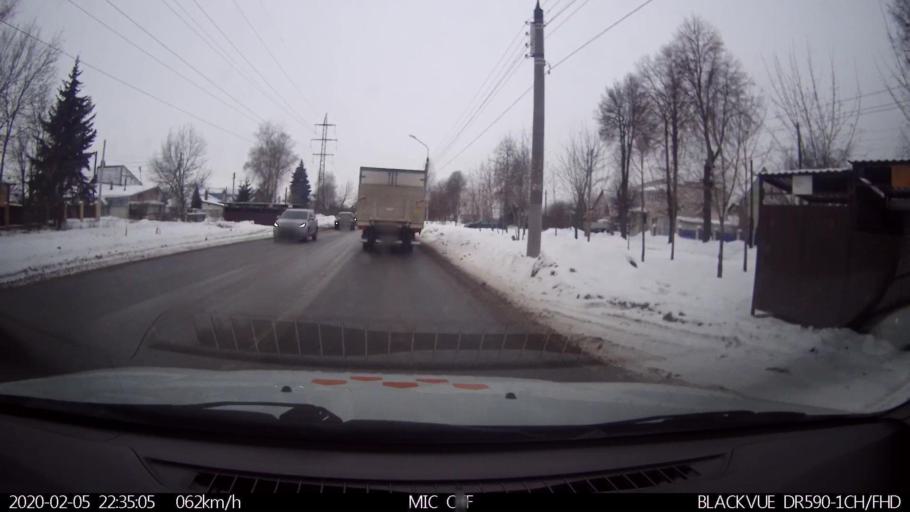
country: RU
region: Nizjnij Novgorod
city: Imeni Stepana Razina
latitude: 54.7351
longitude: 44.2348
